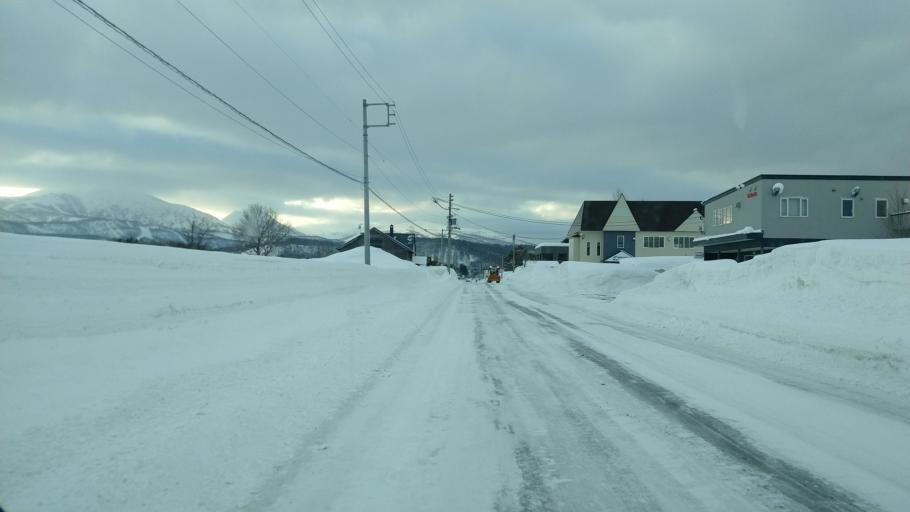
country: JP
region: Hokkaido
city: Niseko Town
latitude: 42.9084
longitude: 140.7638
